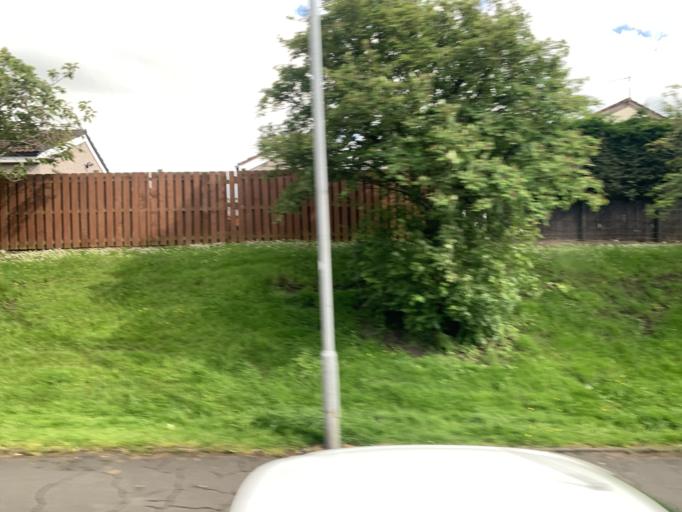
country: GB
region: Scotland
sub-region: South Lanarkshire
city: Uddingston
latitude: 55.8555
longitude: -4.1096
